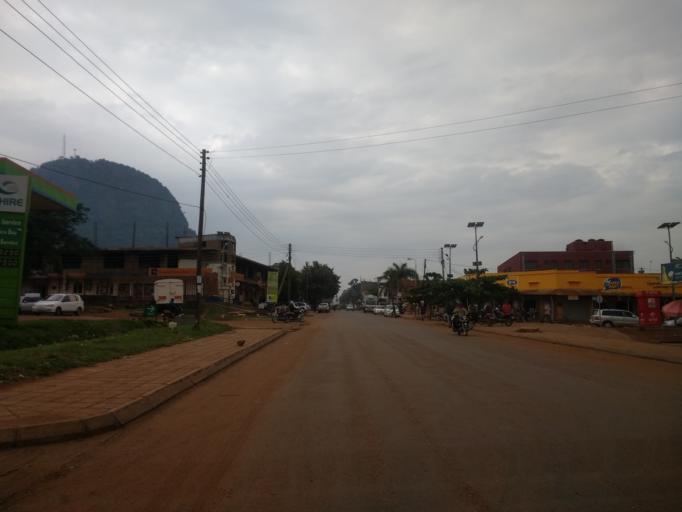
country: UG
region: Eastern Region
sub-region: Tororo District
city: Tororo
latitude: 0.6951
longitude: 34.1815
